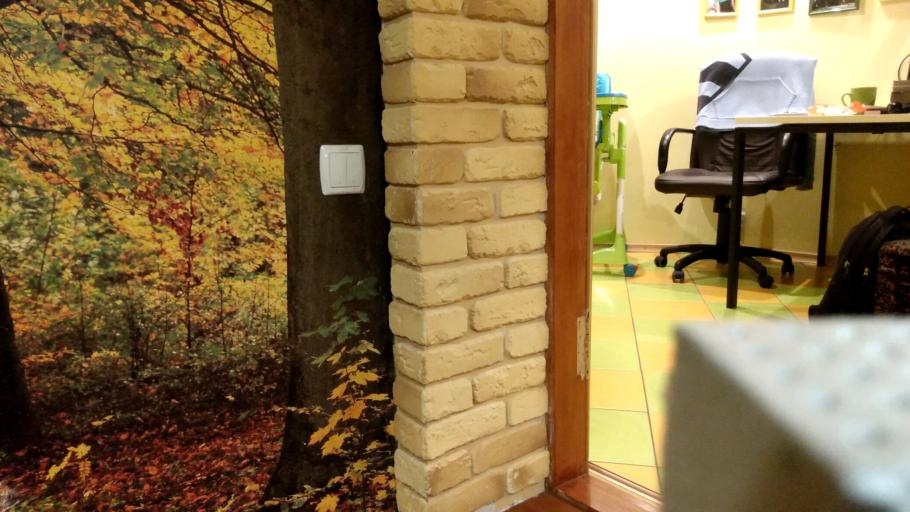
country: RU
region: Republic of Karelia
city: Pudozh
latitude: 61.6402
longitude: 37.7295
